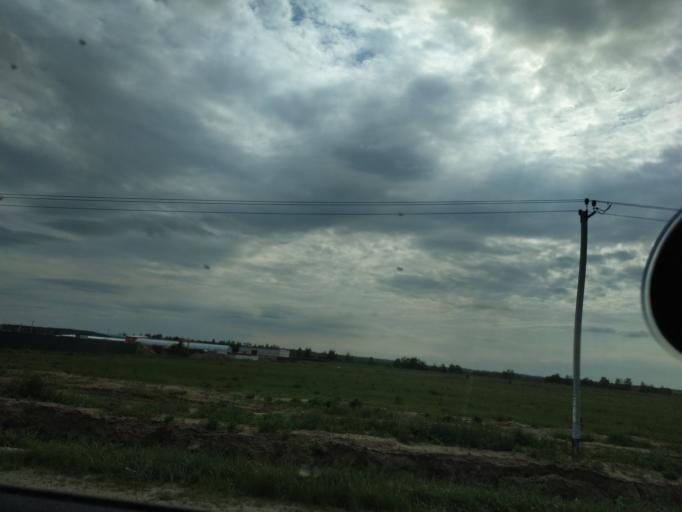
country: RU
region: Moskovskaya
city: Malyshevo
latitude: 55.4952
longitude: 38.3093
